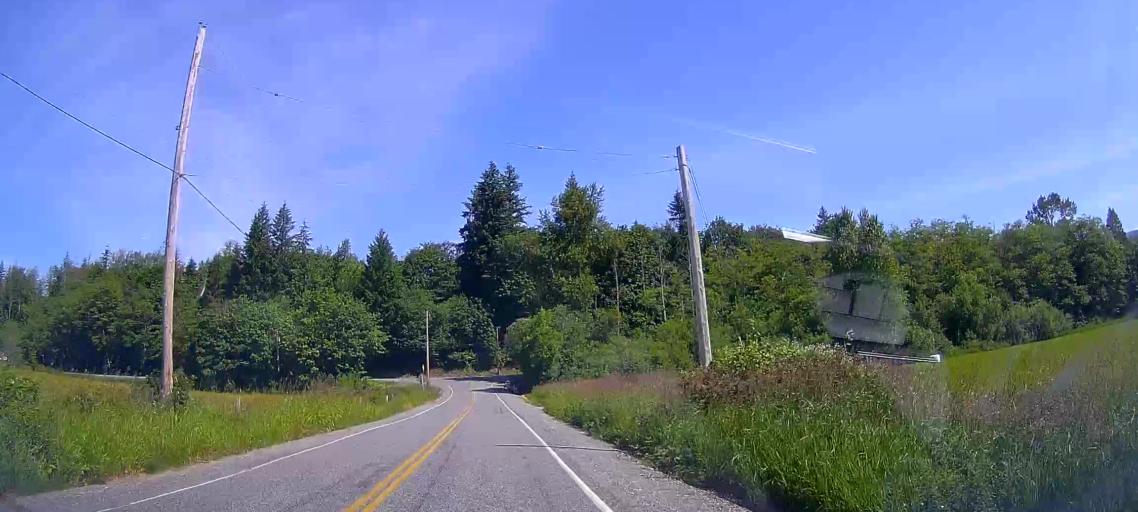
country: US
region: Washington
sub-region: Skagit County
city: Sedro-Woolley
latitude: 48.5537
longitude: -122.2950
